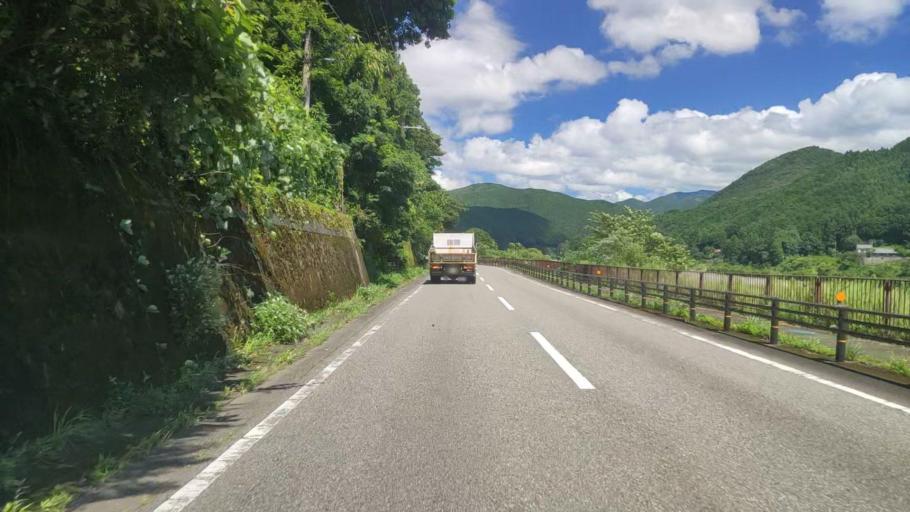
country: JP
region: Wakayama
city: Shingu
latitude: 33.7284
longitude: 135.9503
